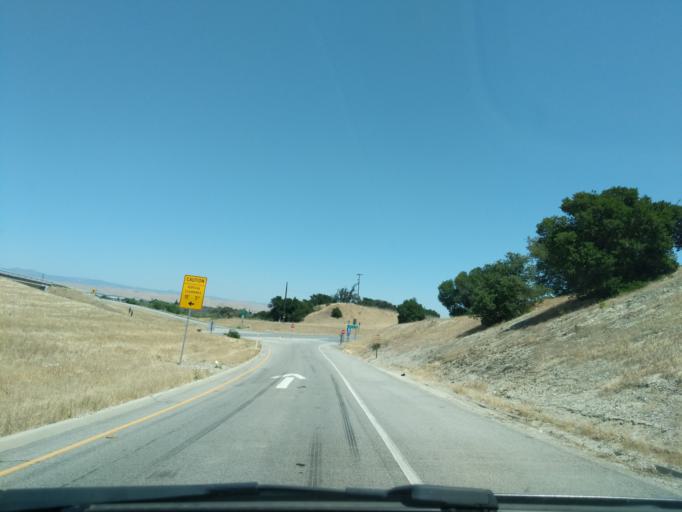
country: US
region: California
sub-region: Monterey County
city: King City
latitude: 36.1970
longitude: -121.1486
